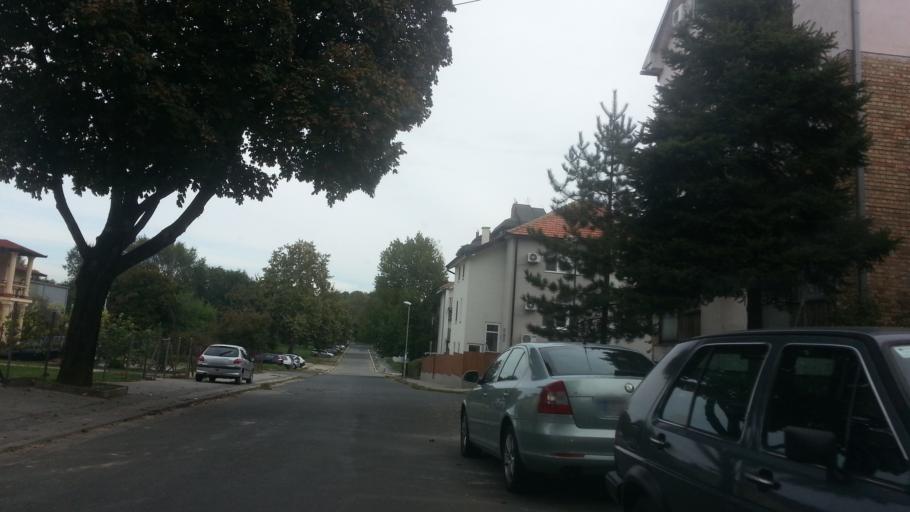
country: RS
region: Central Serbia
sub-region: Belgrade
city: Zemun
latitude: 44.8596
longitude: 20.3674
